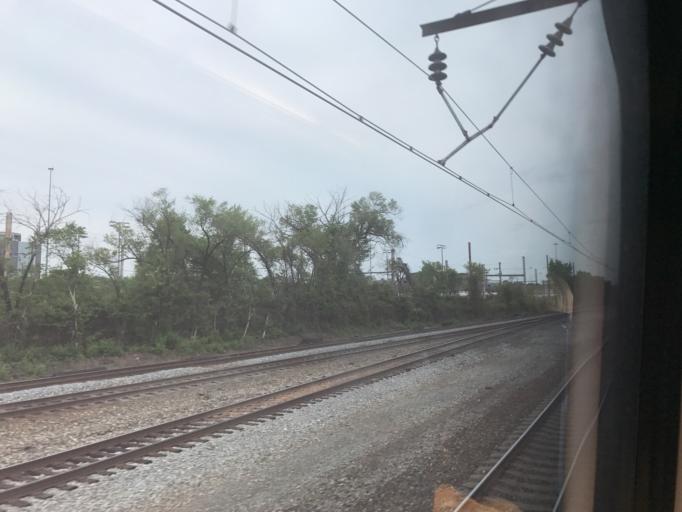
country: US
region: Maryland
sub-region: Prince George's County
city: Mount Rainier
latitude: 38.9138
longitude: -76.9921
